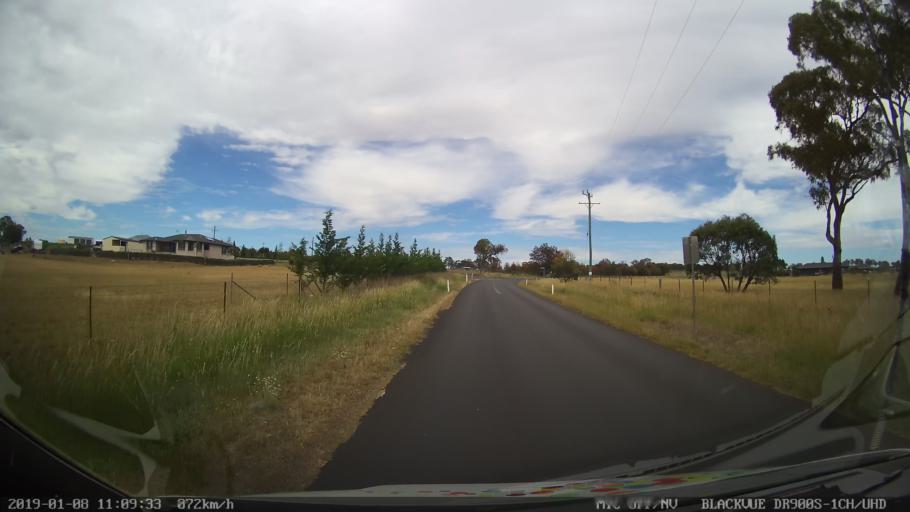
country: AU
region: New South Wales
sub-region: Guyra
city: Guyra
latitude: -30.2261
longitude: 151.6457
